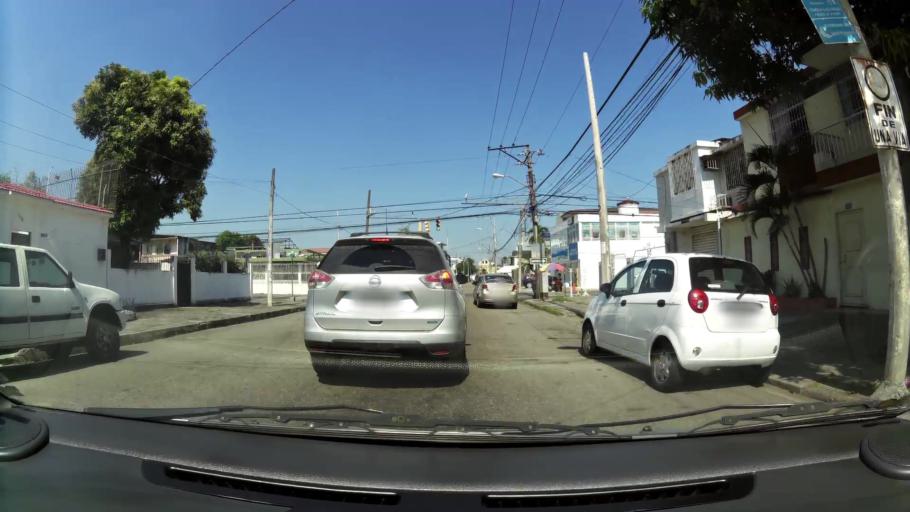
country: EC
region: Guayas
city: Guayaquil
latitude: -2.1644
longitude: -79.9148
